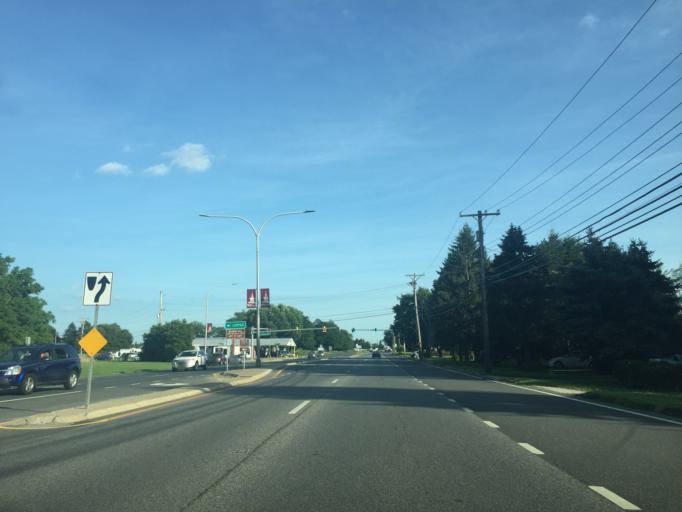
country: US
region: Delaware
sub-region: Kent County
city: Smyrna
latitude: 39.2925
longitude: -75.5972
